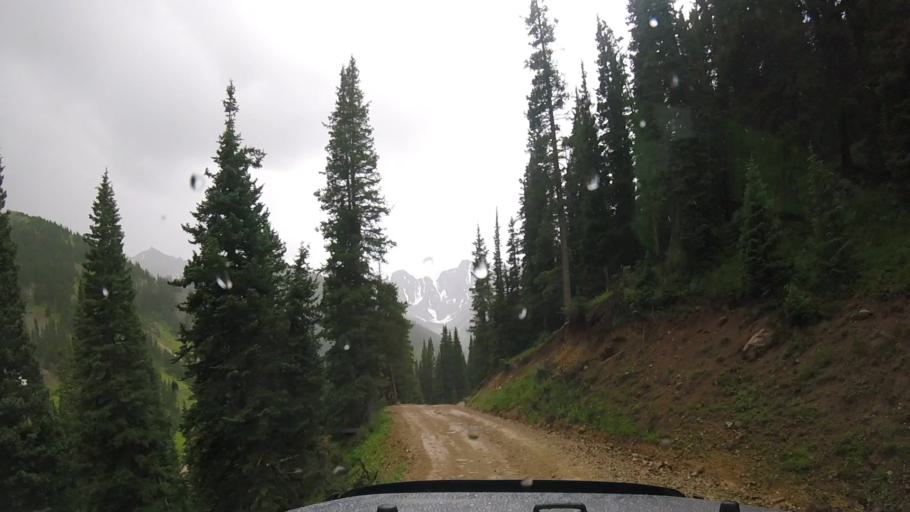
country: US
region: Colorado
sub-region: San Juan County
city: Silverton
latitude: 37.9020
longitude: -107.6472
